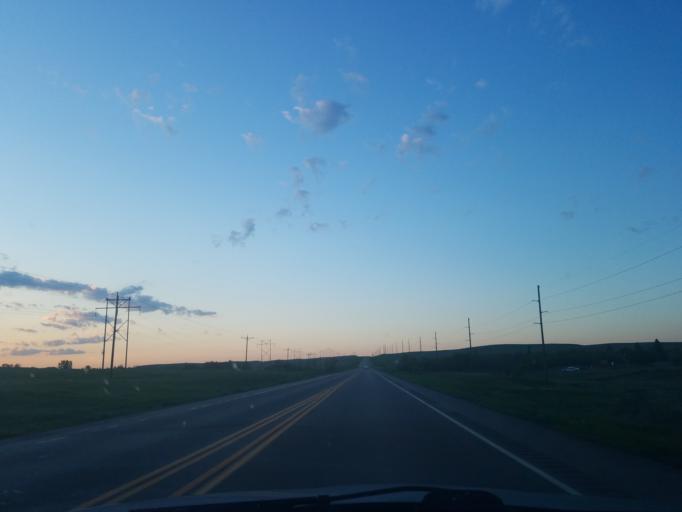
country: US
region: North Dakota
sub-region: McKenzie County
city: Watford City
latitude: 47.7148
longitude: -103.2835
